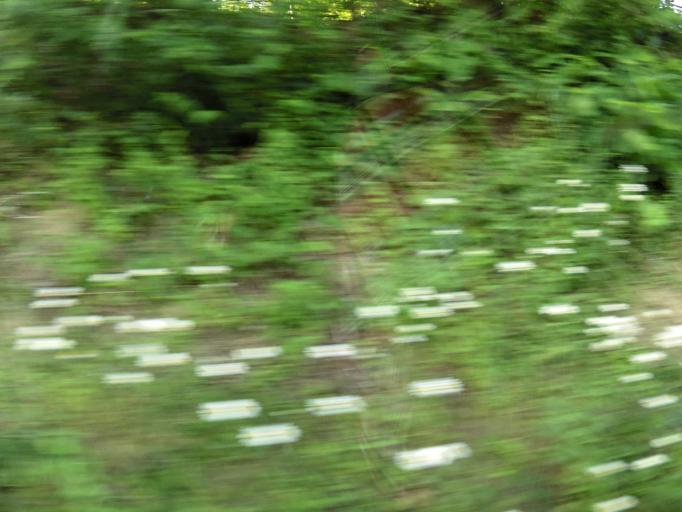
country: US
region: Tennessee
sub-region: Sevier County
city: Sevierville
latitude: 35.8277
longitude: -83.6078
